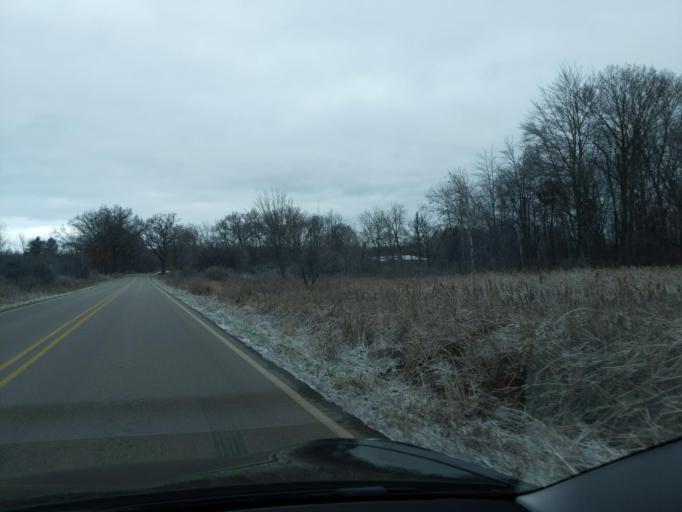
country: US
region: Michigan
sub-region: Jackson County
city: Spring Arbor
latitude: 42.2380
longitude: -84.5174
